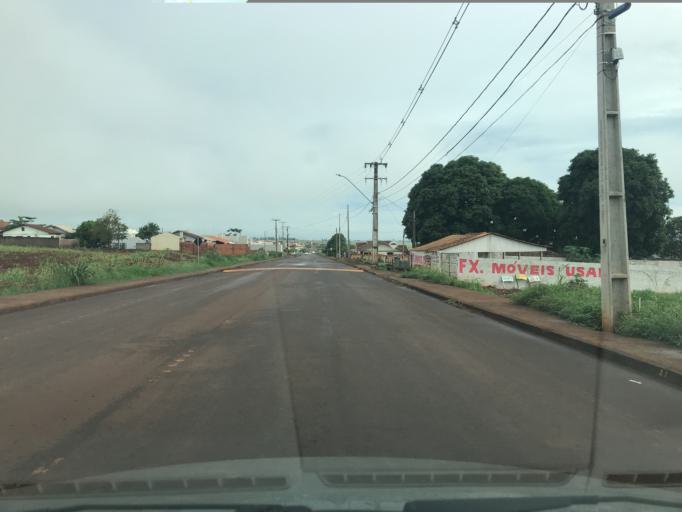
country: BR
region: Parana
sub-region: Palotina
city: Palotina
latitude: -24.2982
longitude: -53.8426
